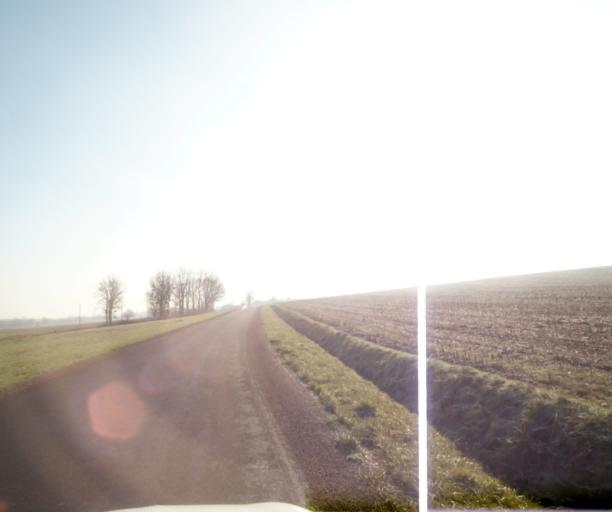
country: FR
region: Champagne-Ardenne
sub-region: Departement de la Haute-Marne
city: Montier-en-Der
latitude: 48.4864
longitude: 4.7413
